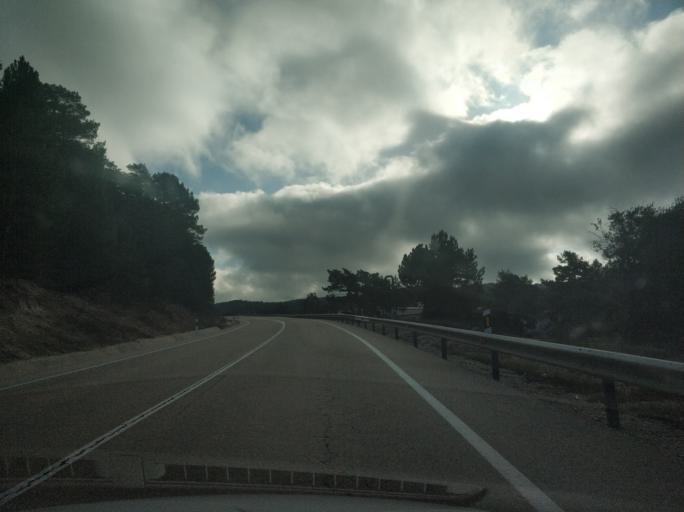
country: ES
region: Castille and Leon
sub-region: Provincia de Soria
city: Navaleno
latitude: 41.8327
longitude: -2.9920
